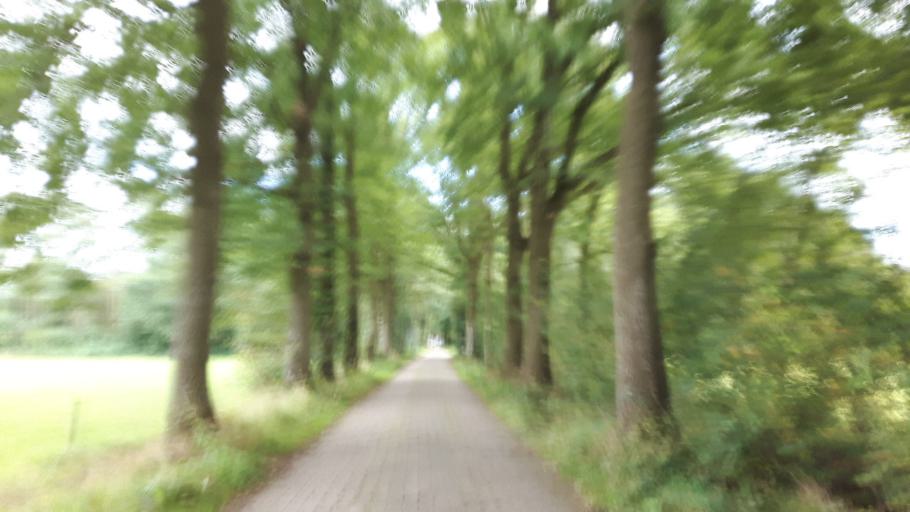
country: NL
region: Friesland
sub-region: Gemeente Smallingerland
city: Drachtstercompagnie
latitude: 53.0640
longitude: 6.2201
